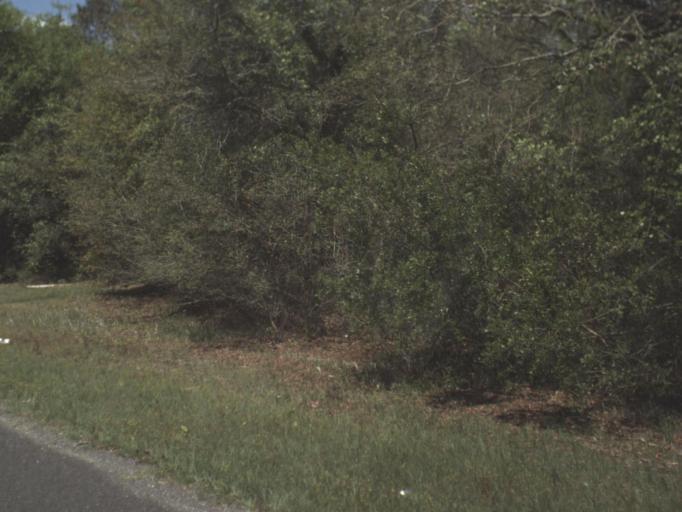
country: US
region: Florida
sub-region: Escambia County
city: Myrtle Grove
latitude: 30.4010
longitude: -87.3823
